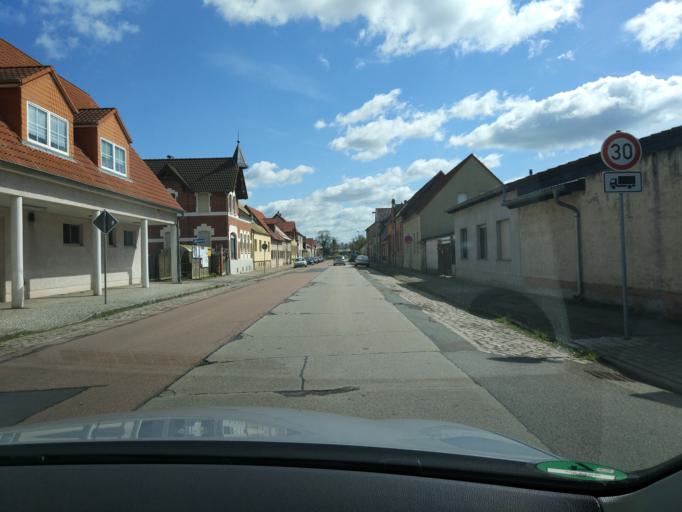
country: DE
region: Saxony-Anhalt
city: Oranienbaum
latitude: 51.7975
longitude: 12.4084
